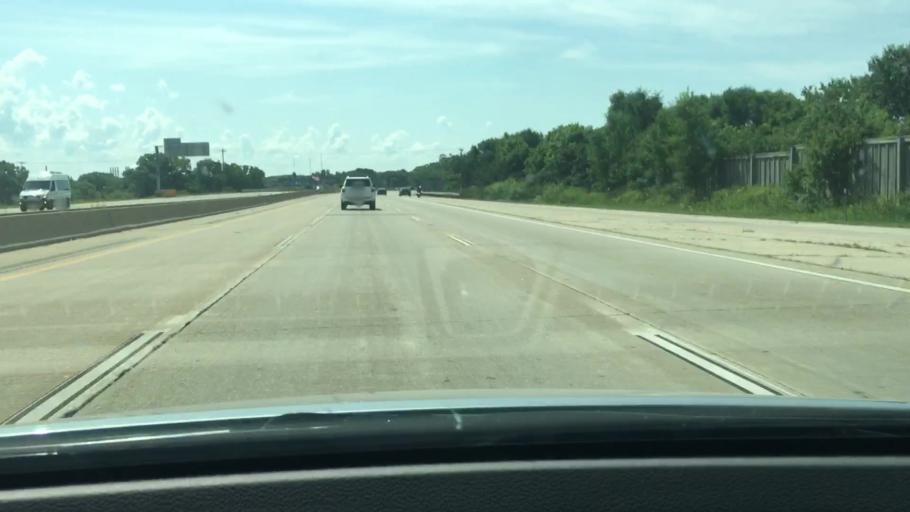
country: US
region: Wisconsin
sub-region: Winnebago County
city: Neenah
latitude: 44.1727
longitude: -88.4874
